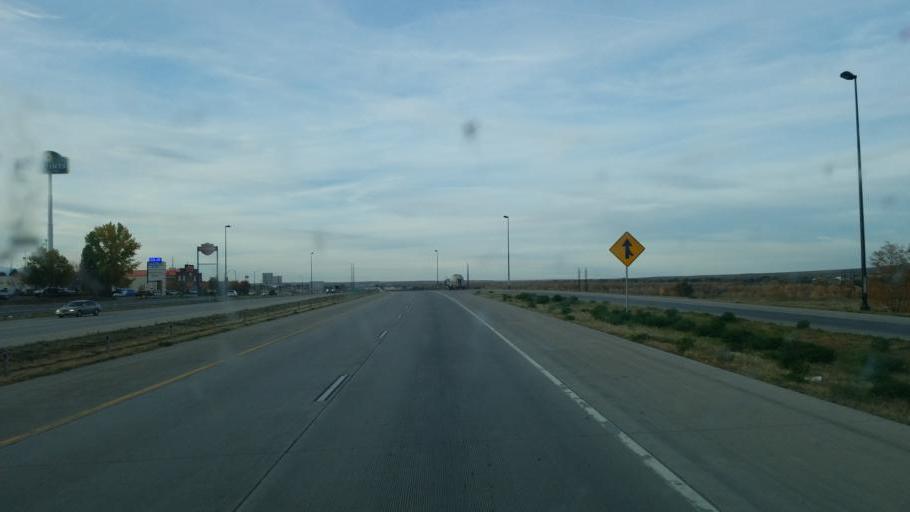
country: US
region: Colorado
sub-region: Pueblo County
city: Pueblo
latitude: 38.3229
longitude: -104.6154
